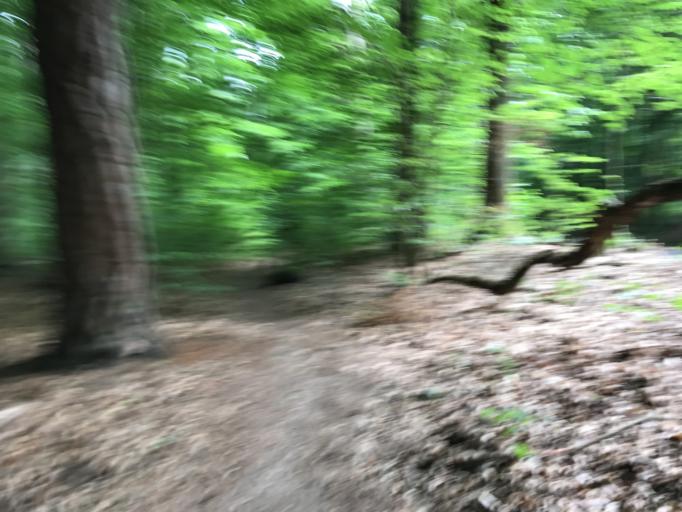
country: DE
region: Hesse
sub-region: Regierungsbezirk Darmstadt
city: Walluf
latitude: 50.0781
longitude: 8.1715
